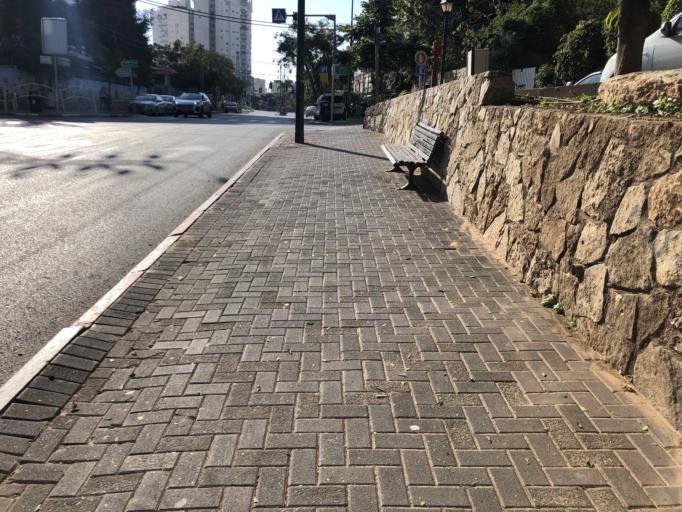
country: IL
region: Tel Aviv
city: Giv`atayim
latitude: 32.0687
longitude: 34.8085
